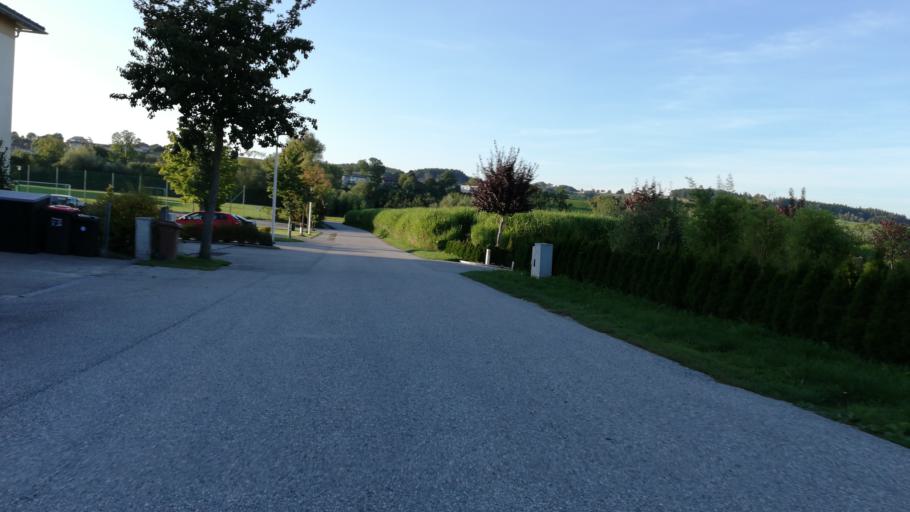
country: AT
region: Upper Austria
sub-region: Politischer Bezirk Grieskirchen
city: Bad Schallerbach
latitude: 48.1853
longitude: 13.9041
